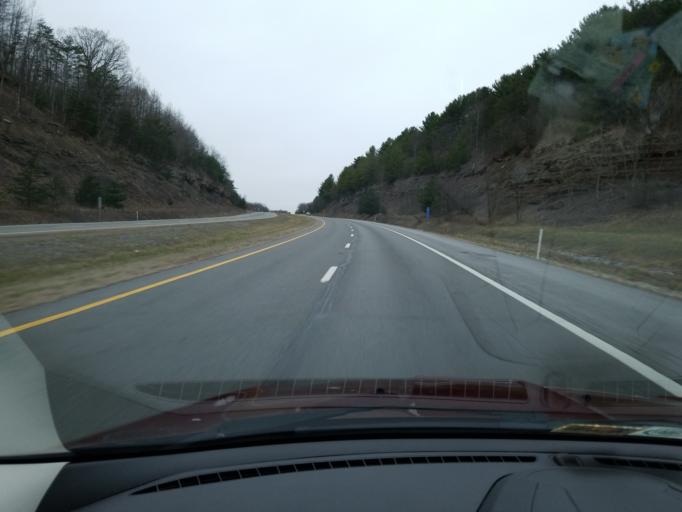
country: US
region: West Virginia
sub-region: Mercer County
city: Athens
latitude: 37.3523
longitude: -81.0160
